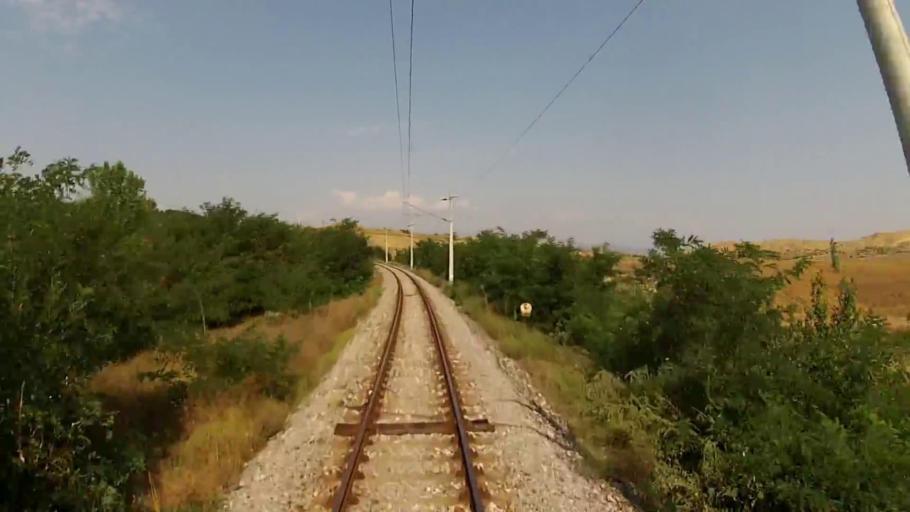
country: BG
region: Blagoevgrad
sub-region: Obshtina Petrich
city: Petrich
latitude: 41.4402
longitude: 23.3104
